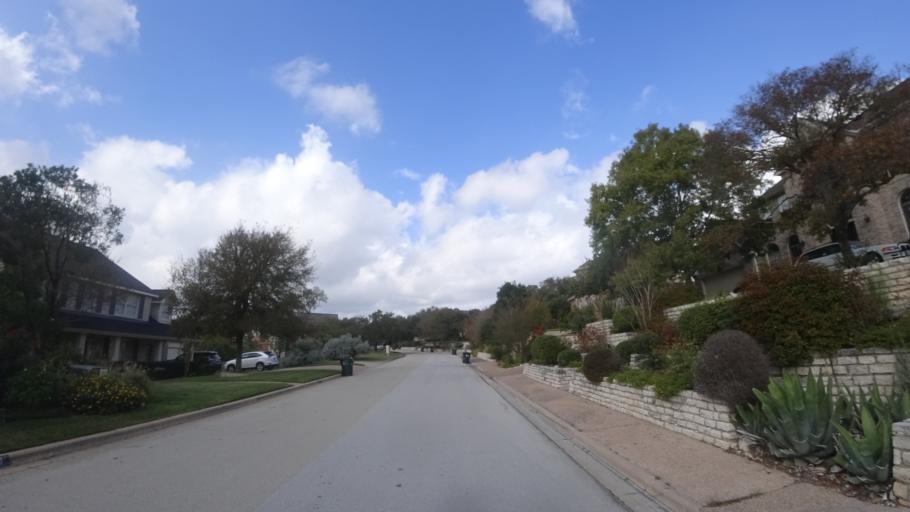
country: US
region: Texas
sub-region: Travis County
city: Barton Creek
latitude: 30.2992
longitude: -97.8833
